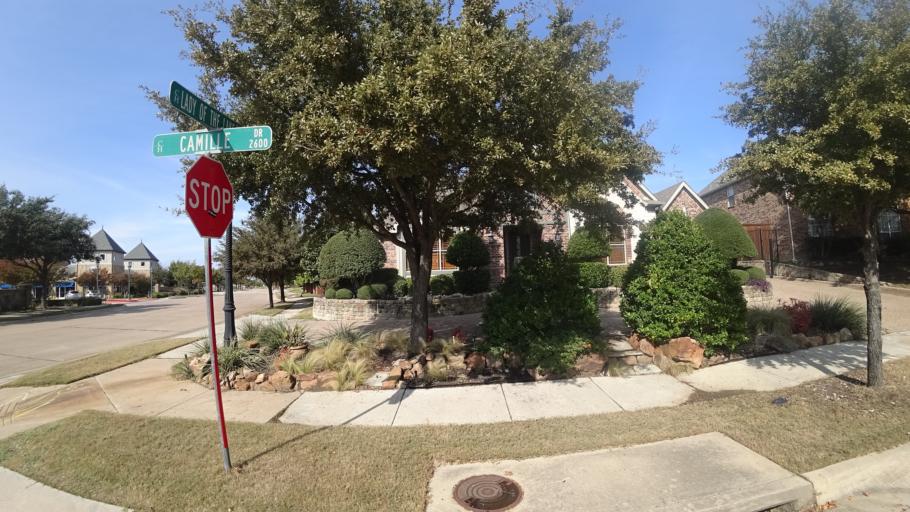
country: US
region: Texas
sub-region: Denton County
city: The Colony
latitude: 33.0356
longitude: -96.8966
